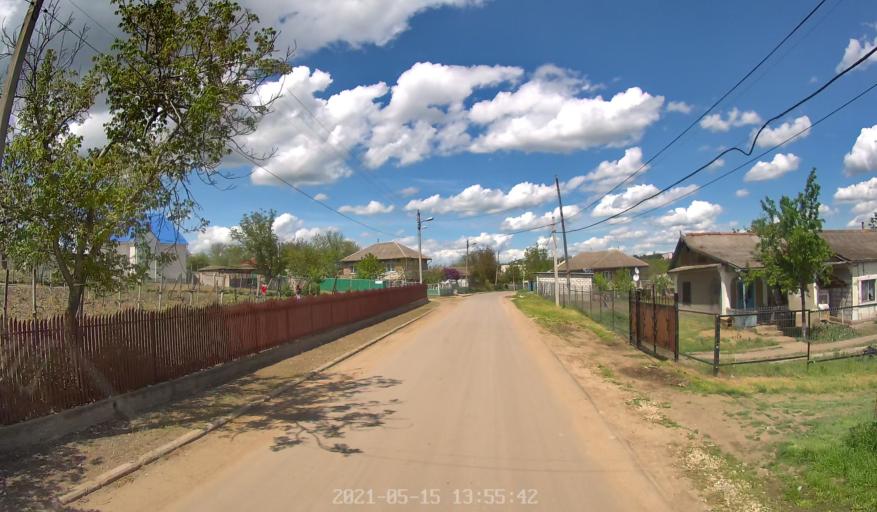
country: MD
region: Hincesti
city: Hincesti
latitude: 46.7339
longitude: 28.5141
